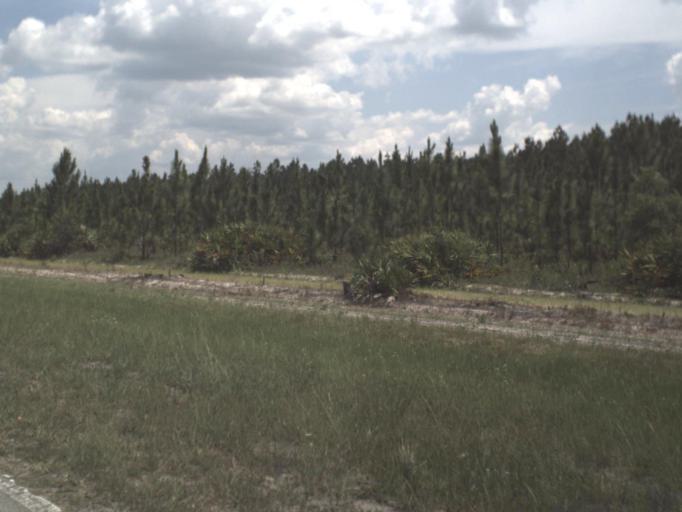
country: US
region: Florida
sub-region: Bradford County
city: Starke
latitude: 29.9943
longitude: -82.0267
